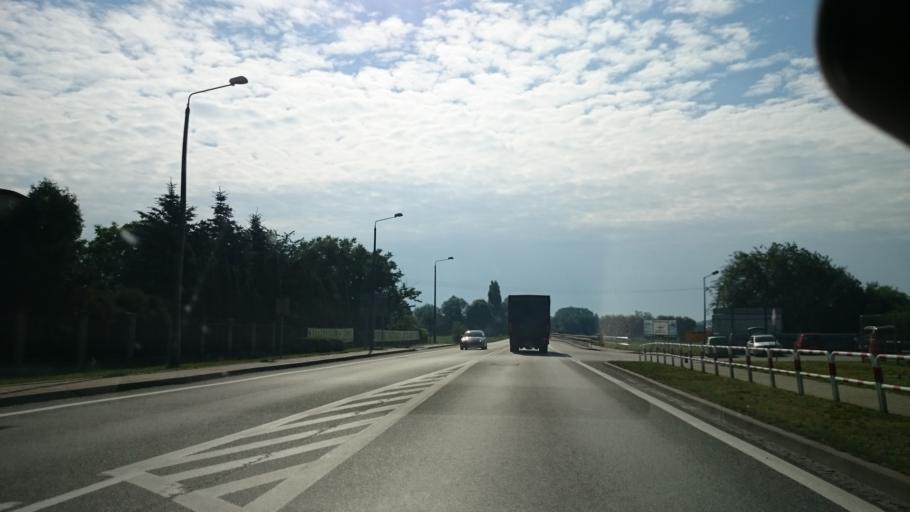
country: PL
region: Opole Voivodeship
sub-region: Powiat strzelecki
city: Strzelce Opolskie
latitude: 50.5067
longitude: 18.3145
